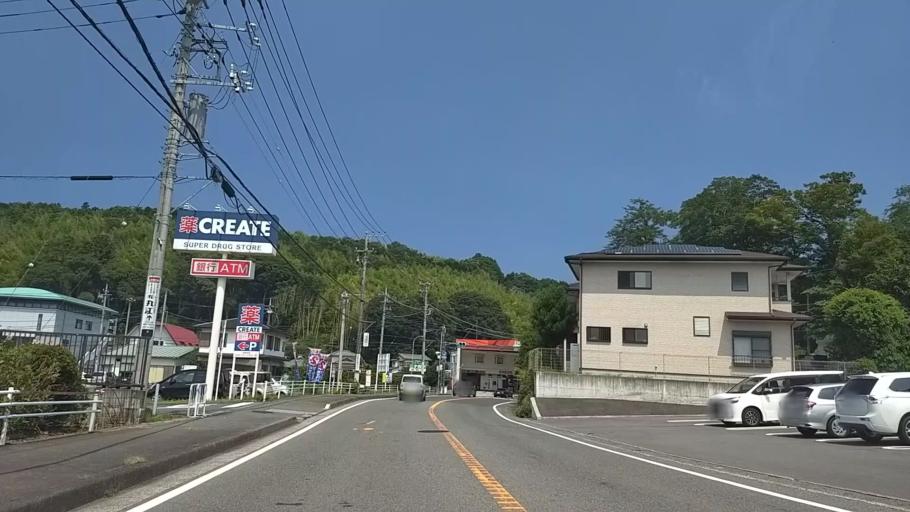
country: JP
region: Shizuoka
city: Ito
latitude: 34.9358
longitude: 139.0901
